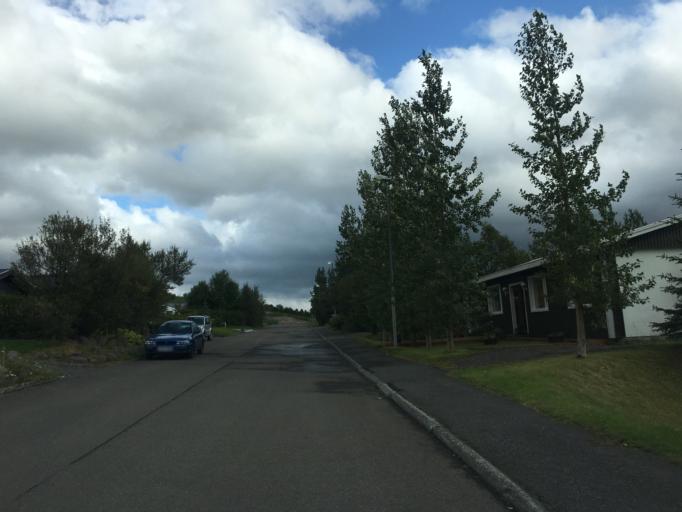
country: IS
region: East
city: Reydarfjoerdur
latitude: 65.0357
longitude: -14.2089
